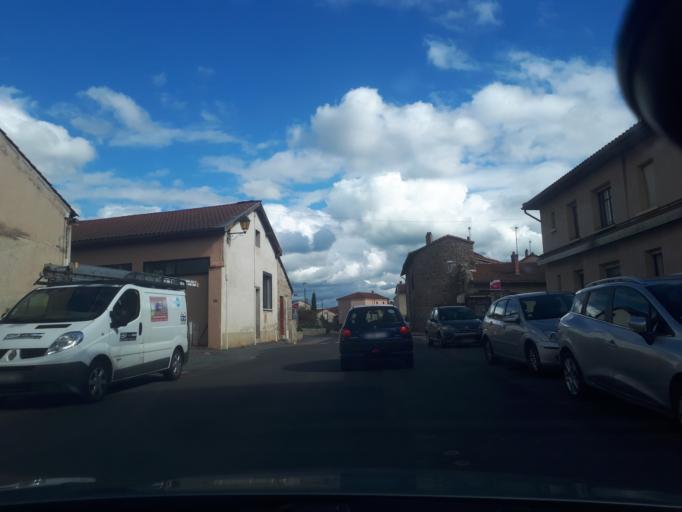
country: FR
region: Rhone-Alpes
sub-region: Departement de la Loire
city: Pouilly-les-Feurs
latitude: 45.7991
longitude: 4.2313
